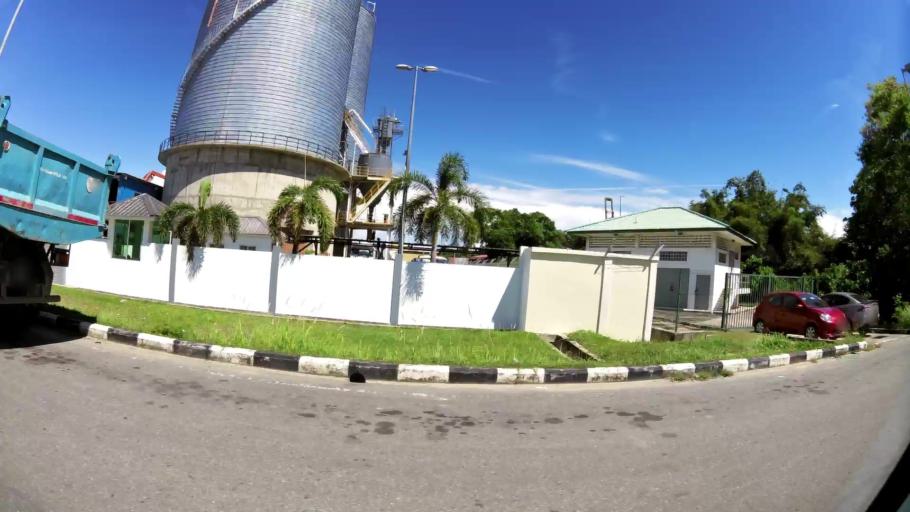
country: BN
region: Brunei and Muara
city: Bandar Seri Begawan
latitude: 5.0276
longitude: 115.0703
